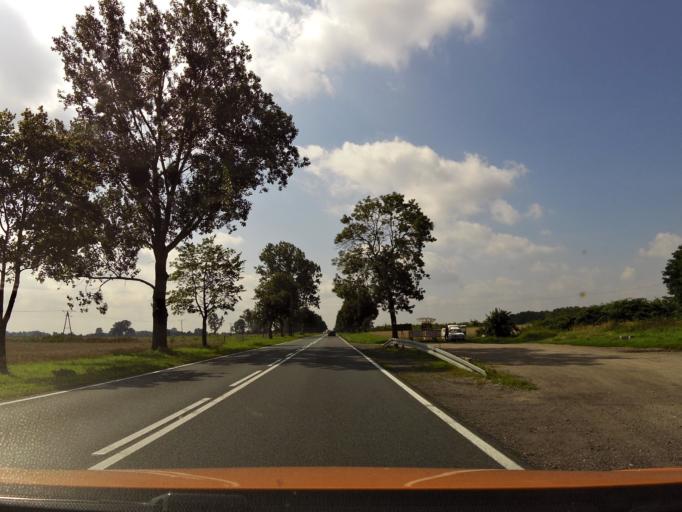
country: PL
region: West Pomeranian Voivodeship
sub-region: Powiat gryficki
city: Ploty
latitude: 53.7356
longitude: 15.2062
